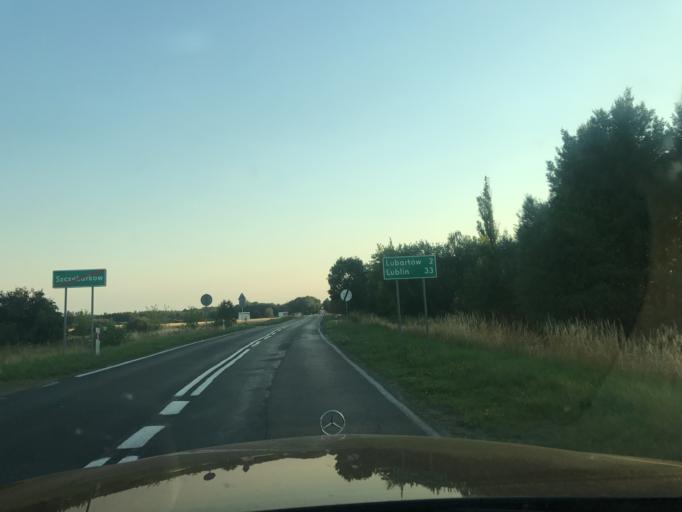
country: PL
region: Lublin Voivodeship
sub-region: Powiat lubartowski
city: Lubartow
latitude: 51.4824
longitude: 22.6238
